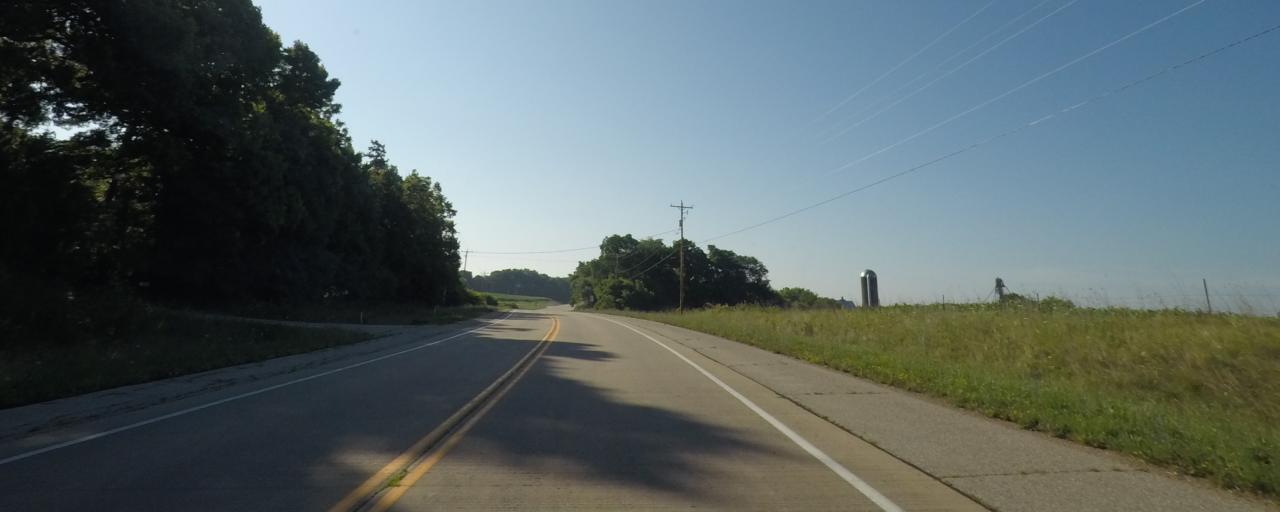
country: US
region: Wisconsin
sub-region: Jefferson County
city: Lake Koshkonong
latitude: 42.9613
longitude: -88.8959
